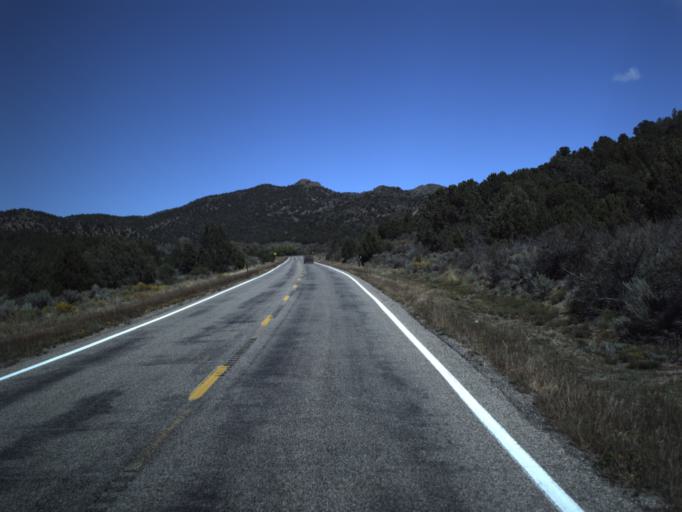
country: US
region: Utah
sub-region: Washington County
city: Enterprise
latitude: 37.4460
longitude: -113.6246
